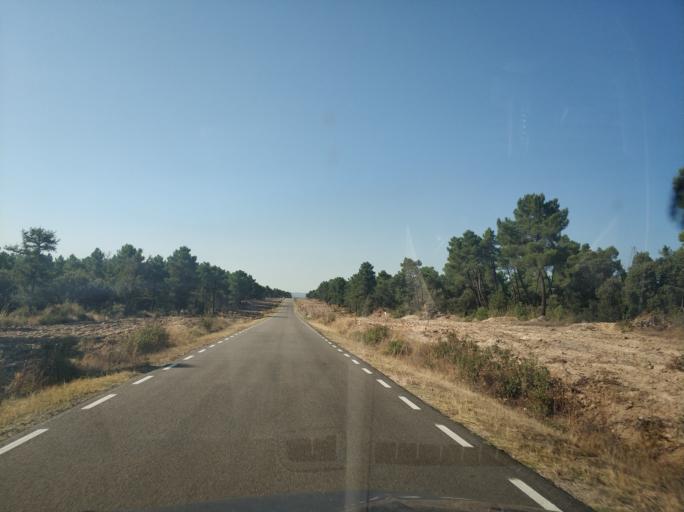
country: ES
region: Castille and Leon
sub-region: Provincia de Burgos
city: San Juan del Monte
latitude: 41.6682
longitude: -3.5280
